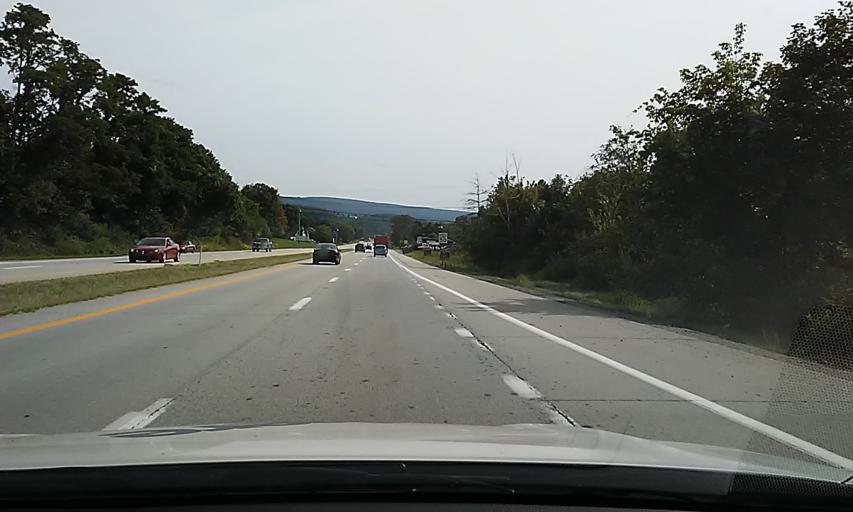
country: US
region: Pennsylvania
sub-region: Westmoreland County
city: Scottdale
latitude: 40.0702
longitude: -79.5652
